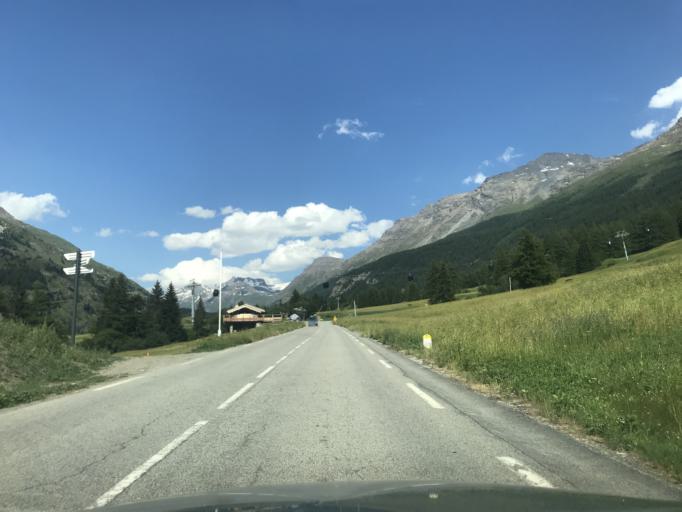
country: IT
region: Piedmont
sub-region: Provincia di Torino
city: Moncenisio
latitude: 45.2845
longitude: 6.9054
